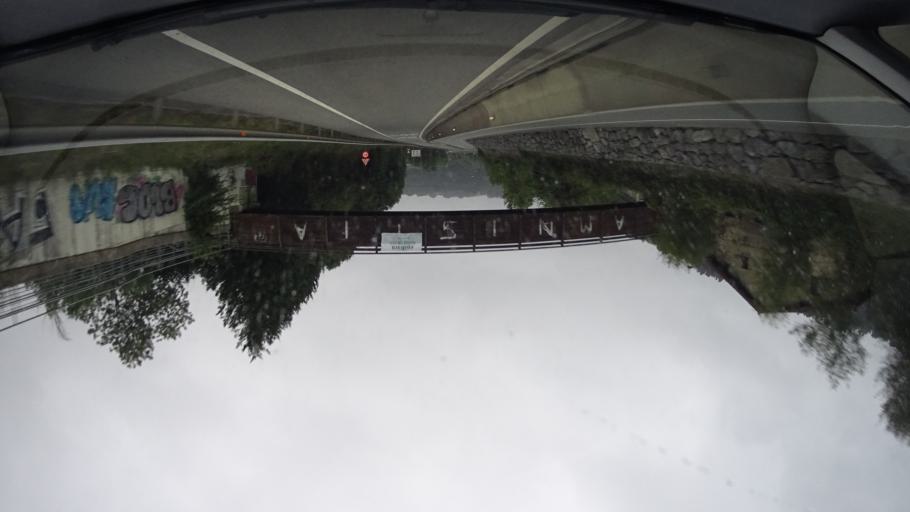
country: ES
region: Basque Country
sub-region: Bizkaia
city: Durango
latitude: 43.1657
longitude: -2.6372
